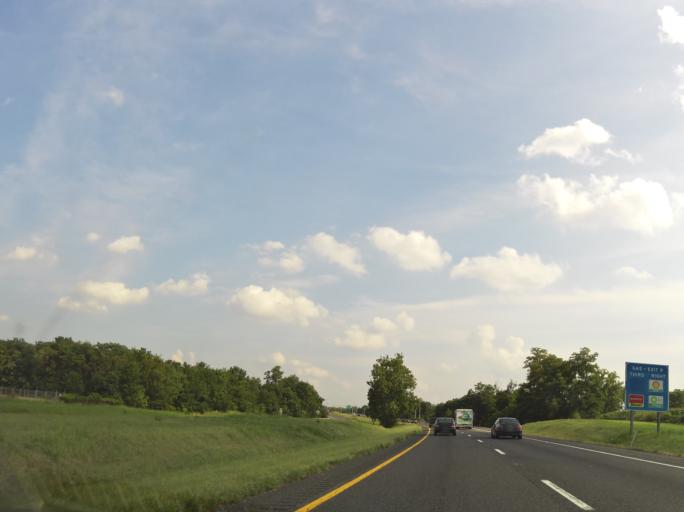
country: US
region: Maryland
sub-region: Washington County
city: Maugansville
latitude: 39.7061
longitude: -77.7428
